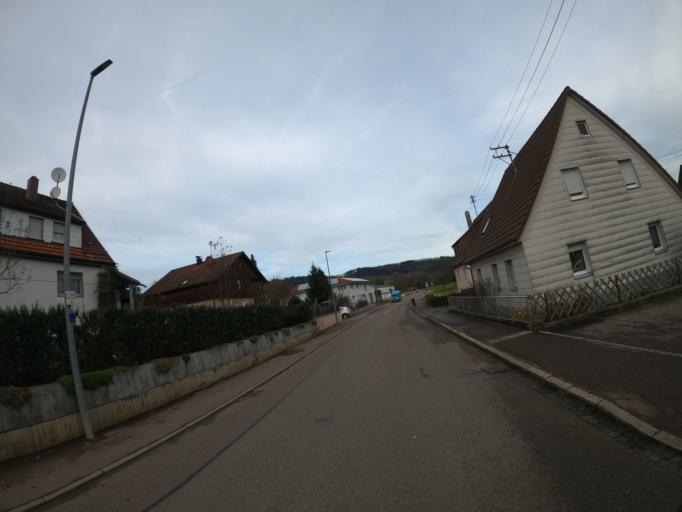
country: DE
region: Baden-Wuerttemberg
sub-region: Regierungsbezirk Stuttgart
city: Ottenbach
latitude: 48.7381
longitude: 9.7495
